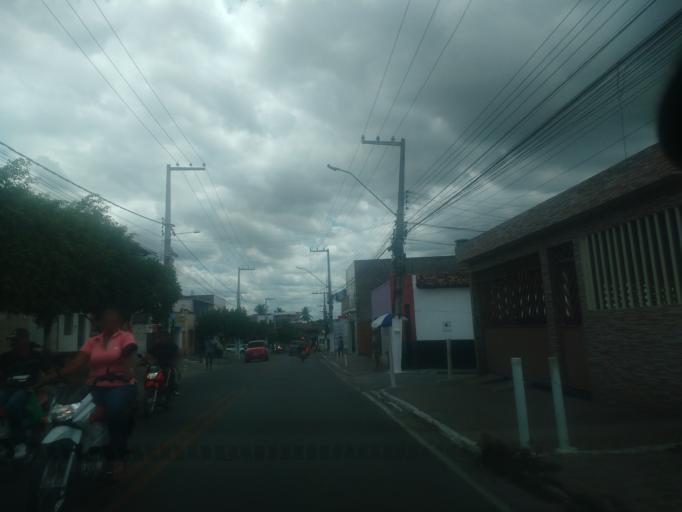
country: BR
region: Alagoas
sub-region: Uniao Dos Palmares
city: Uniao dos Palmares
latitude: -9.1557
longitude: -36.0252
